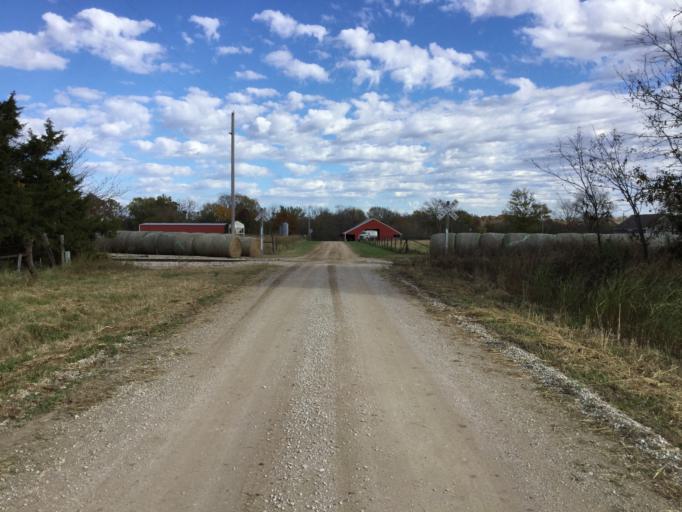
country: US
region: Kansas
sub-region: Montgomery County
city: Cherryvale
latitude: 37.1659
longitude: -95.5889
